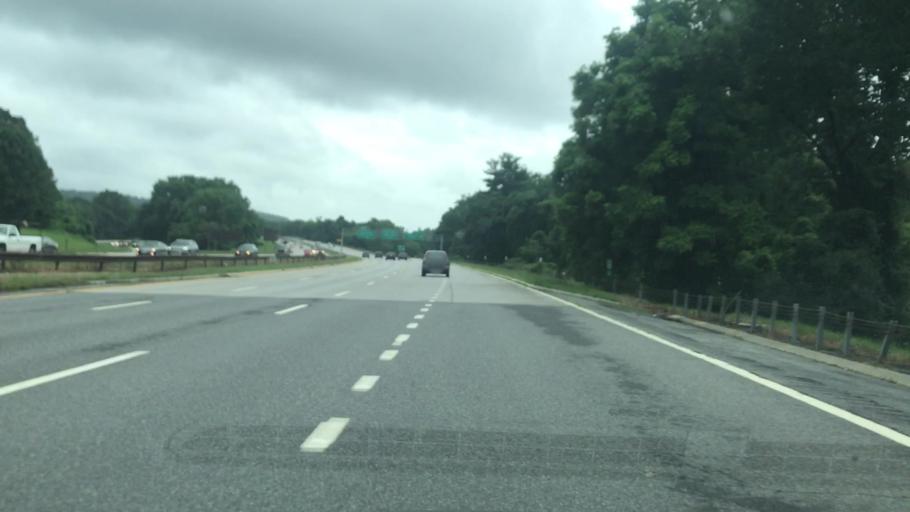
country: US
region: New York
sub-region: Westchester County
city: Hawthorne
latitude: 41.1147
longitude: -73.8057
